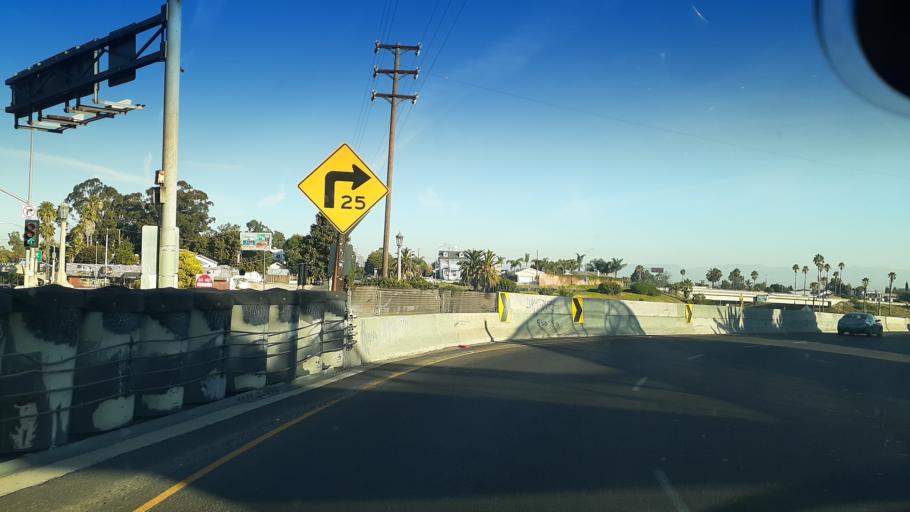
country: US
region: California
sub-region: Los Angeles County
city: San Pedro
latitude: 33.7465
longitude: -118.2923
